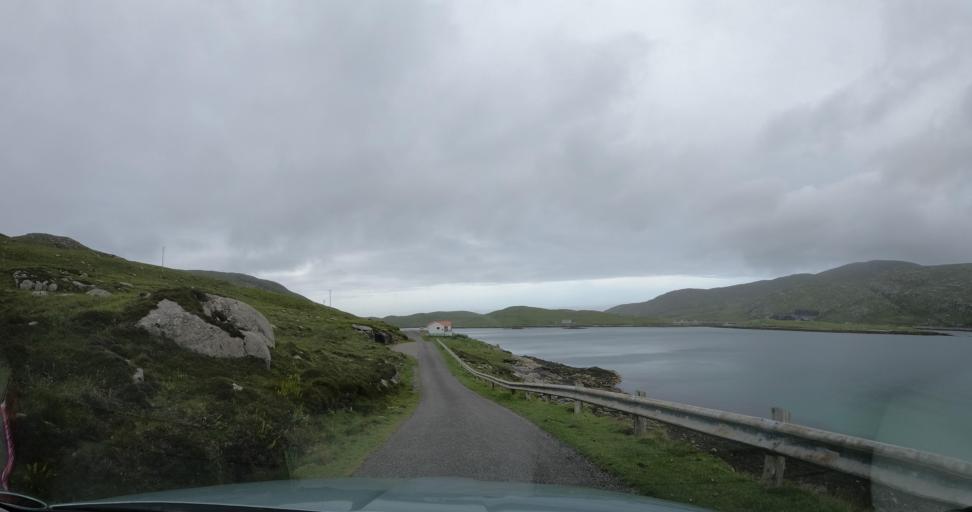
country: GB
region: Scotland
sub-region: Eilean Siar
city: Barra
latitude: 56.9367
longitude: -7.5218
